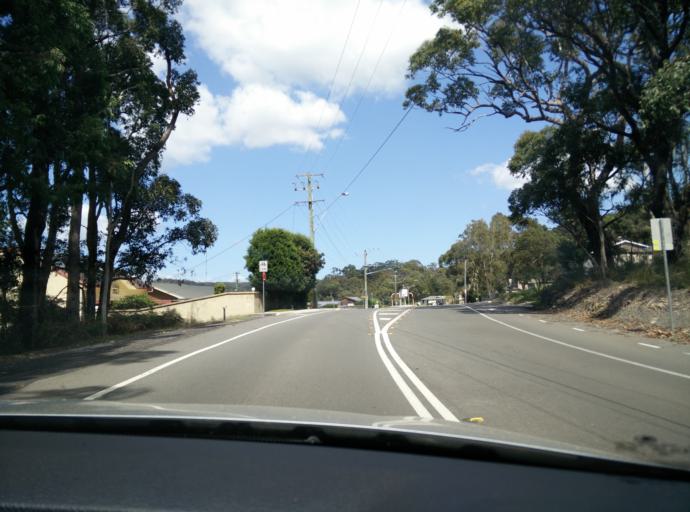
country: AU
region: New South Wales
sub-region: Gosford Shire
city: Blackwall
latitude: -33.4886
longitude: 151.3017
